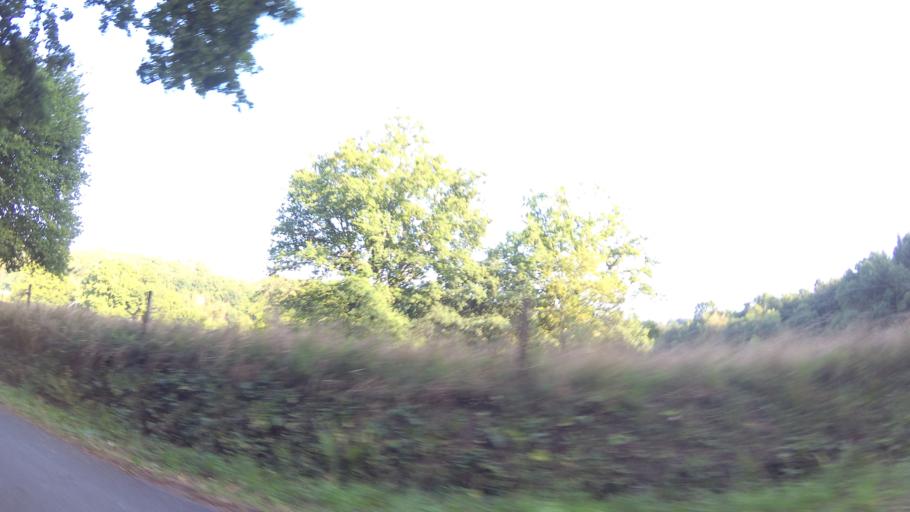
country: DE
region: Saarland
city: Blieskastel
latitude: 49.2356
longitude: 7.2307
